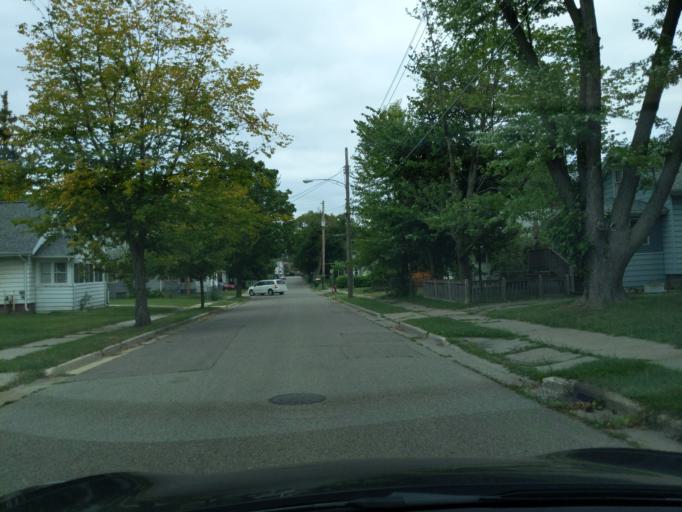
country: US
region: Michigan
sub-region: Ingham County
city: Lansing
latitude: 42.7233
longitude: -84.5319
